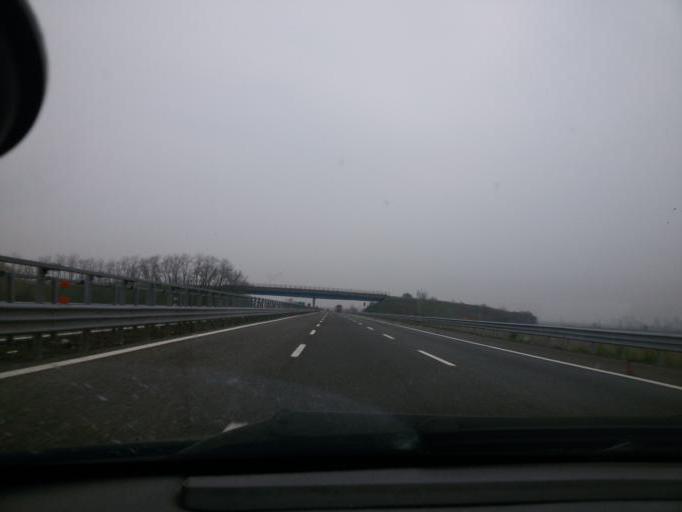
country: IT
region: Piedmont
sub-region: Provincia di Alessandria
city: Villanova Monferrato
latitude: 45.1900
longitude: 8.4953
